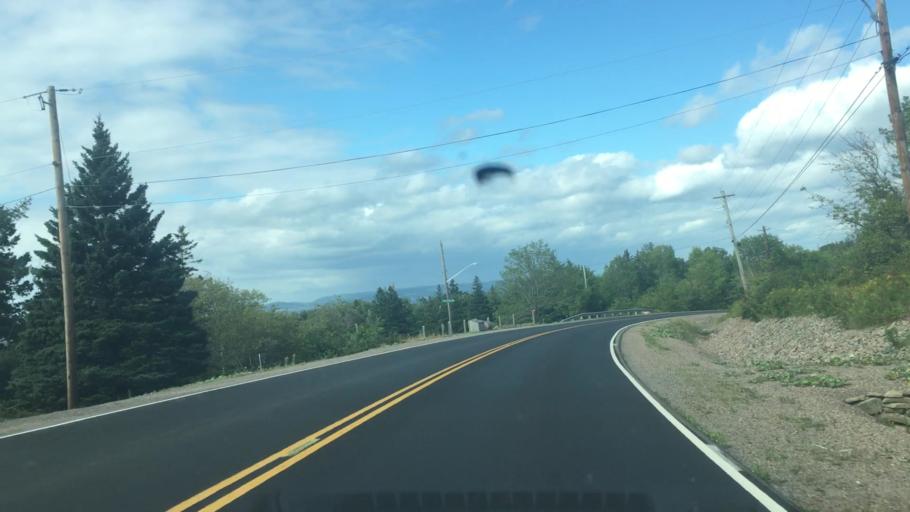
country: CA
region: Nova Scotia
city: Princeville
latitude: 45.7902
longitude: -60.7403
